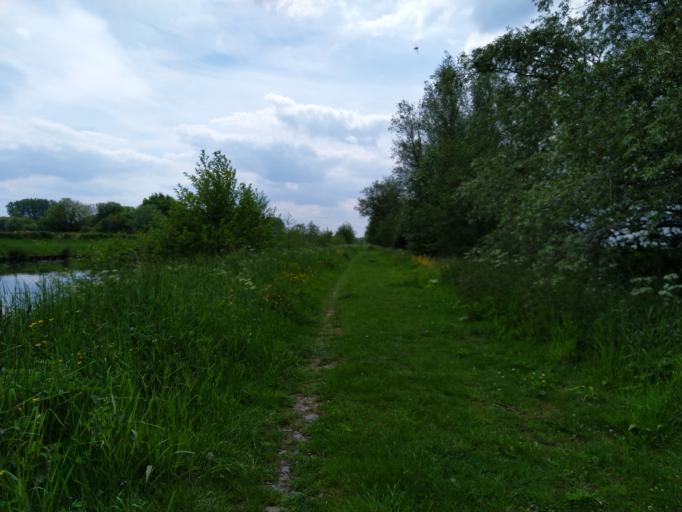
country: FR
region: Nord-Pas-de-Calais
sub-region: Departement du Nord
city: Landrecies
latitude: 50.1206
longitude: 3.6790
